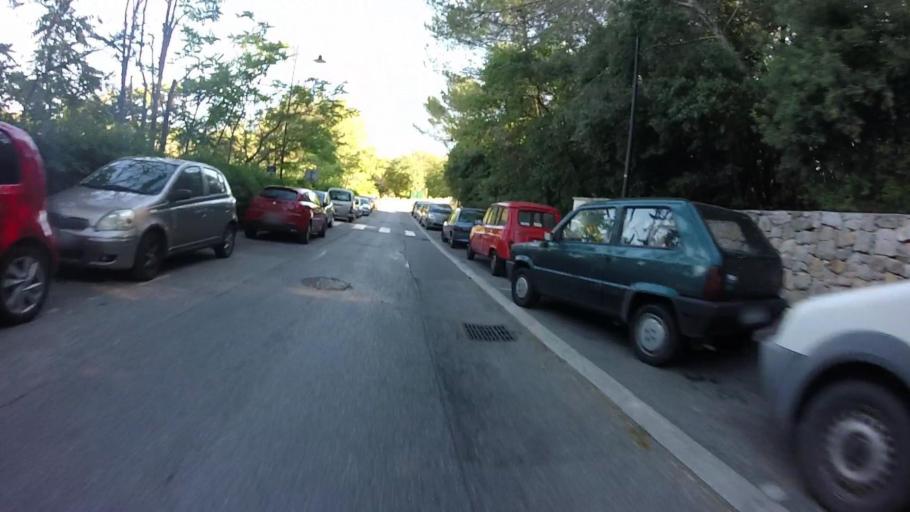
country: FR
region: Provence-Alpes-Cote d'Azur
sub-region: Departement des Alpes-Maritimes
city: Vallauris
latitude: 43.6207
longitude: 7.0474
